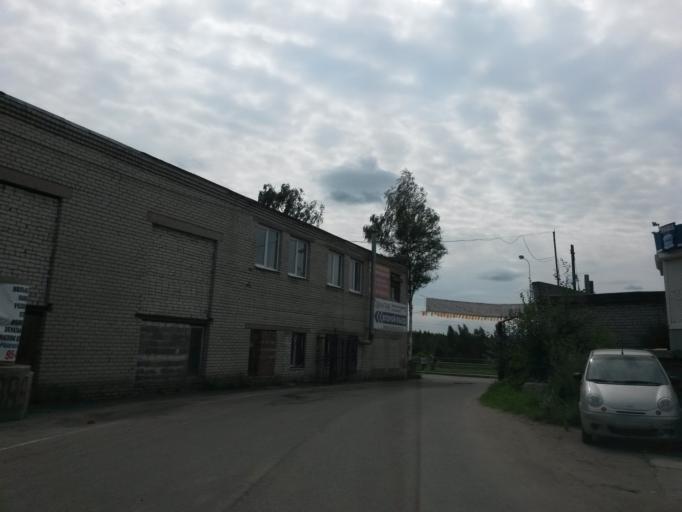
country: RU
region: Jaroslavl
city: Yaroslavl
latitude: 57.6857
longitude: 39.9070
